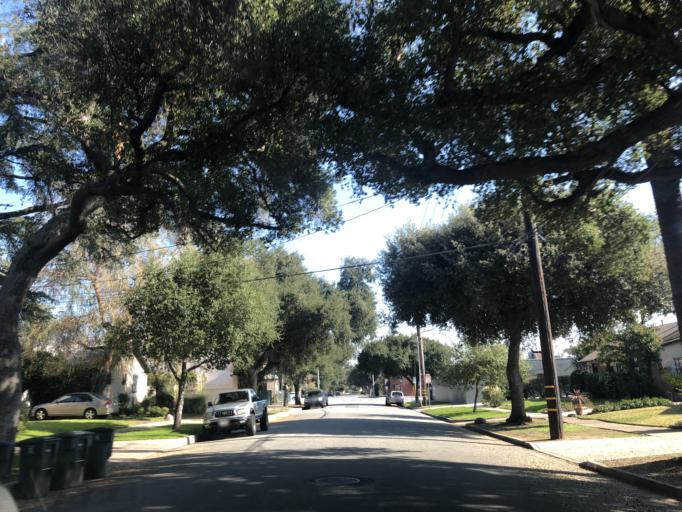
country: US
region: California
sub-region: Los Angeles County
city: East Pasadena
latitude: 34.1508
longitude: -118.1146
